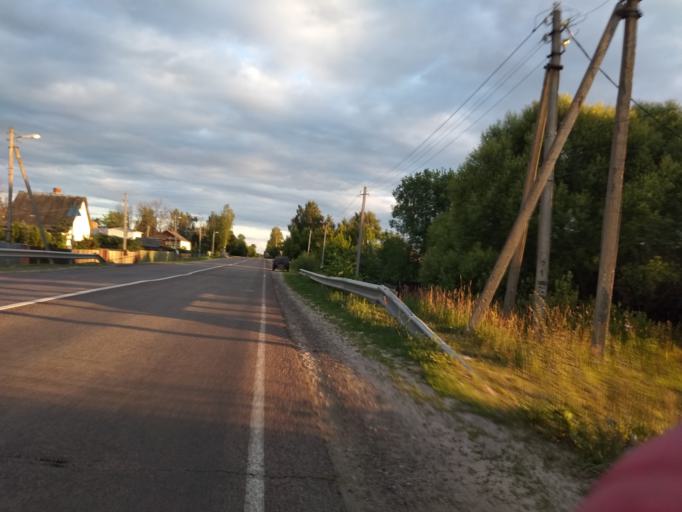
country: RU
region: Moskovskaya
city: Misheronskiy
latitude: 55.6011
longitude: 39.7061
